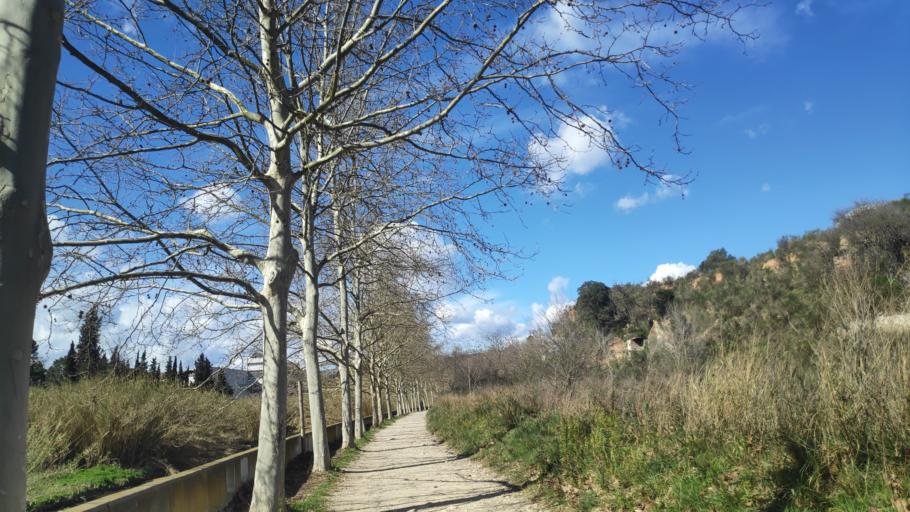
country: ES
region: Catalonia
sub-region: Provincia de Barcelona
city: Sabadell
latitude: 41.5579
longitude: 2.1149
